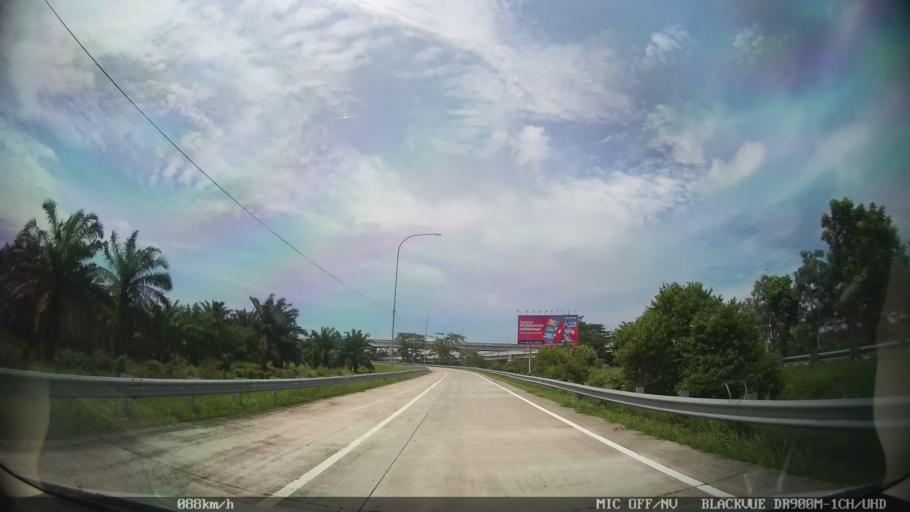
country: ID
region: North Sumatra
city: Percut
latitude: 3.6008
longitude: 98.8449
